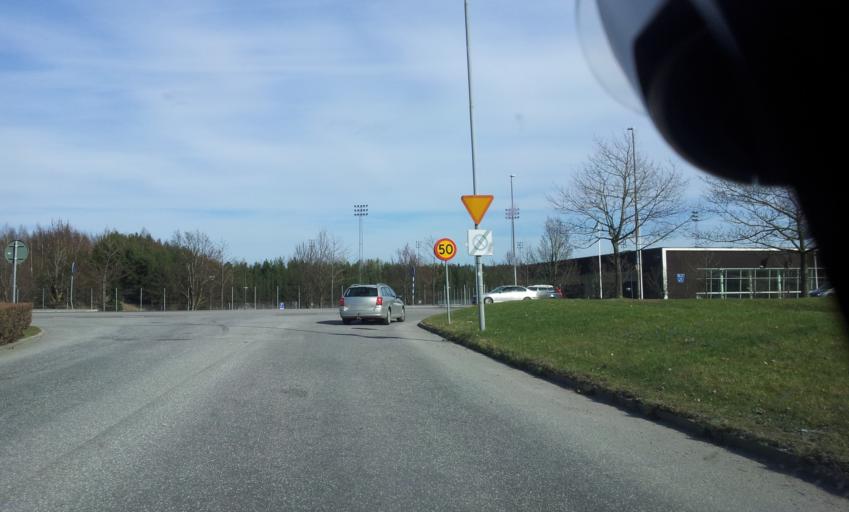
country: SE
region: Stockholm
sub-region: Upplands Vasby Kommun
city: Upplands Vaesby
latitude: 59.5178
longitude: 17.9171
